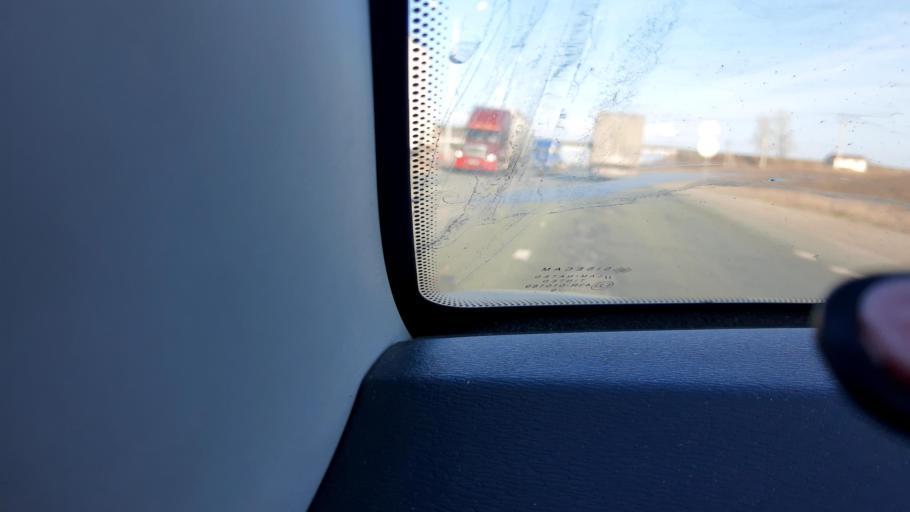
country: RU
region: Bashkortostan
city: Avdon
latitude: 54.6424
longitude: 55.5631
